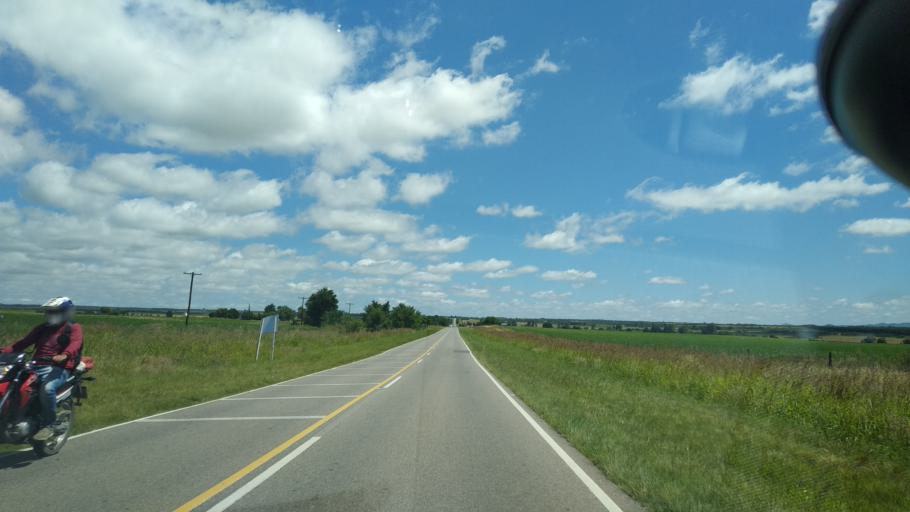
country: AR
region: Cordoba
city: Villa Cura Brochero
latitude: -31.6509
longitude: -65.0996
